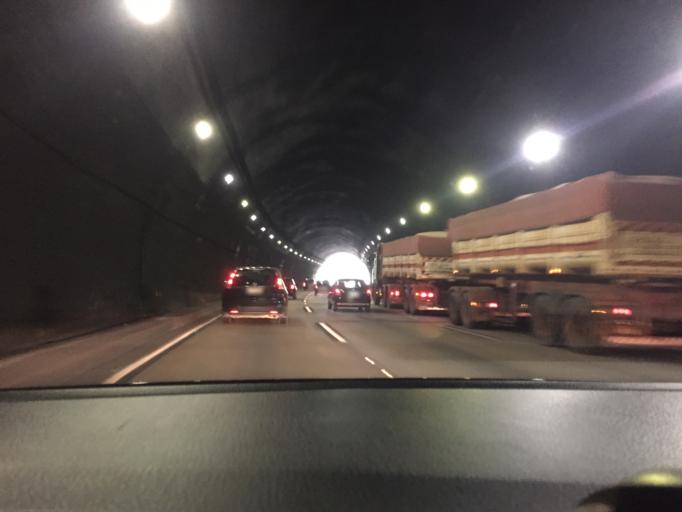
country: BR
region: Sao Paulo
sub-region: Cubatao
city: Cubatao
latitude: -23.8936
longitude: -46.5052
